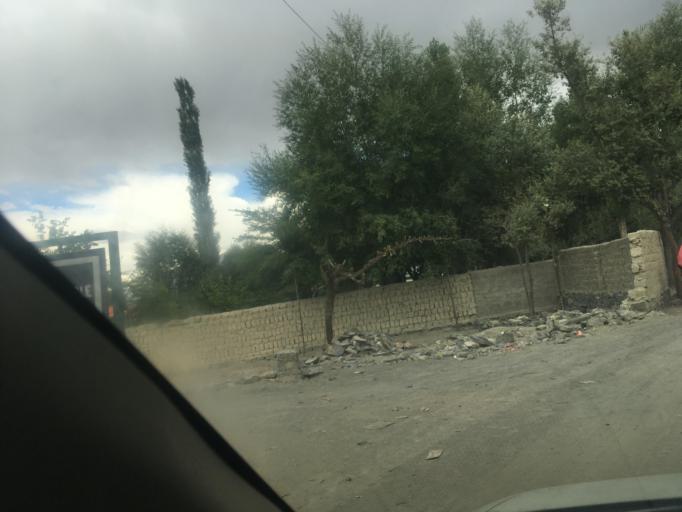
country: PK
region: Gilgit-Baltistan
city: Skardu
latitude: 35.3177
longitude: 75.5502
